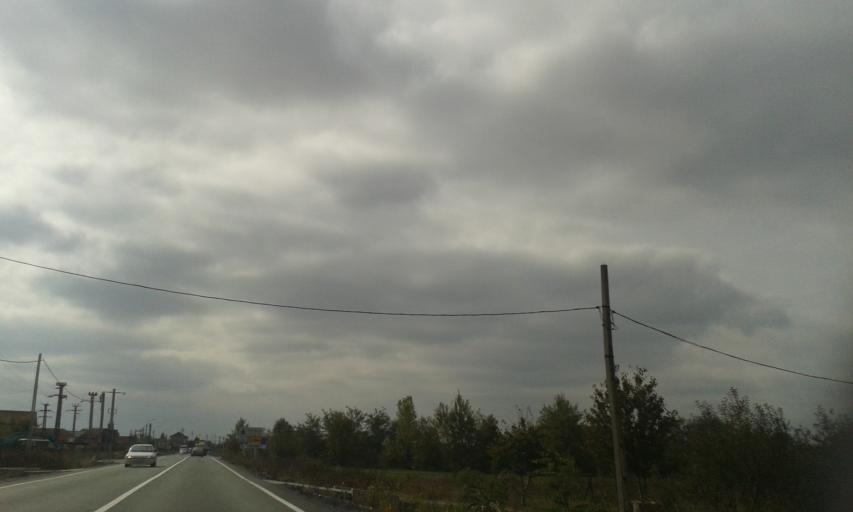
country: RO
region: Gorj
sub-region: Comuna Turcinesti
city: Turcinesti
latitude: 45.1037
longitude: 23.3379
